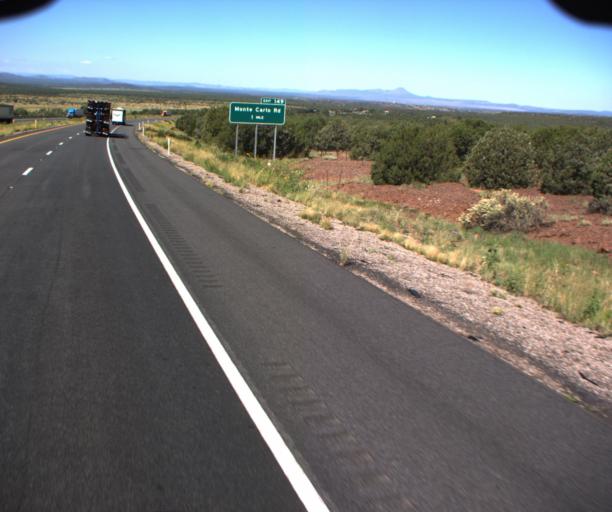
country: US
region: Arizona
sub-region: Coconino County
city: Williams
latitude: 35.2146
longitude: -112.4043
